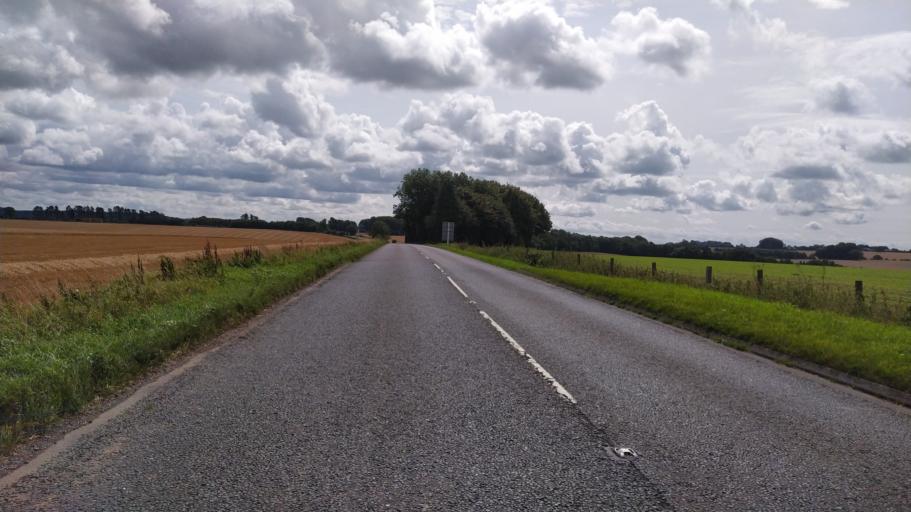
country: GB
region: England
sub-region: Wiltshire
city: Chicklade
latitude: 51.1155
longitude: -2.1693
